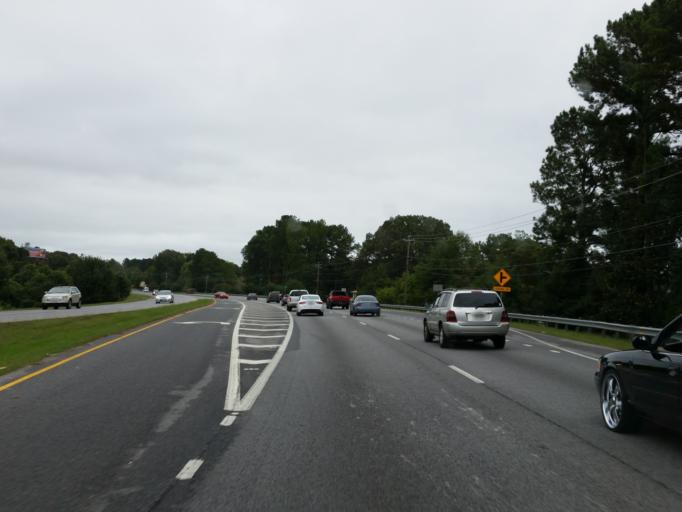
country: US
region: Georgia
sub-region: Clayton County
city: Bonanza
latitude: 33.4651
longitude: -84.3350
